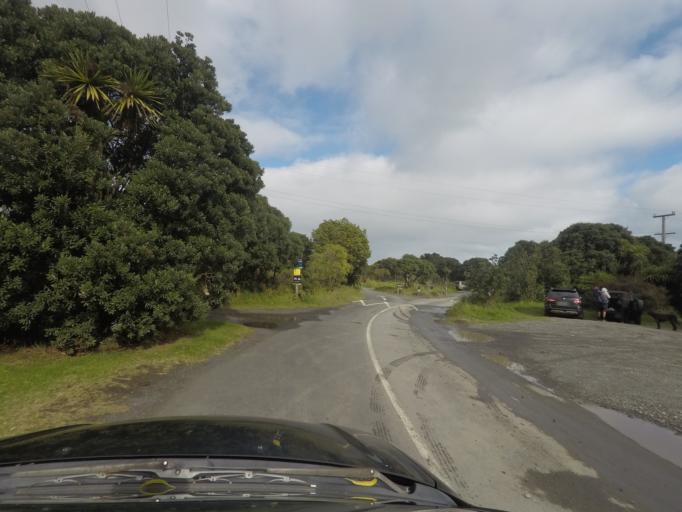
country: NZ
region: Auckland
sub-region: Auckland
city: Muriwai Beach
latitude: -36.8905
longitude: 174.4495
